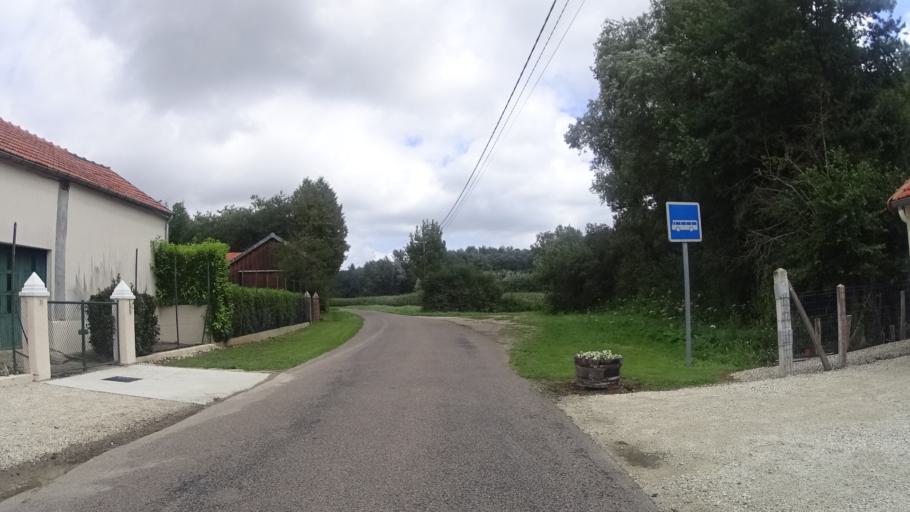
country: FR
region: Champagne-Ardenne
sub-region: Departement de l'Aube
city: Ervy-le-Chatel
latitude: 48.0652
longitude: 3.9462
